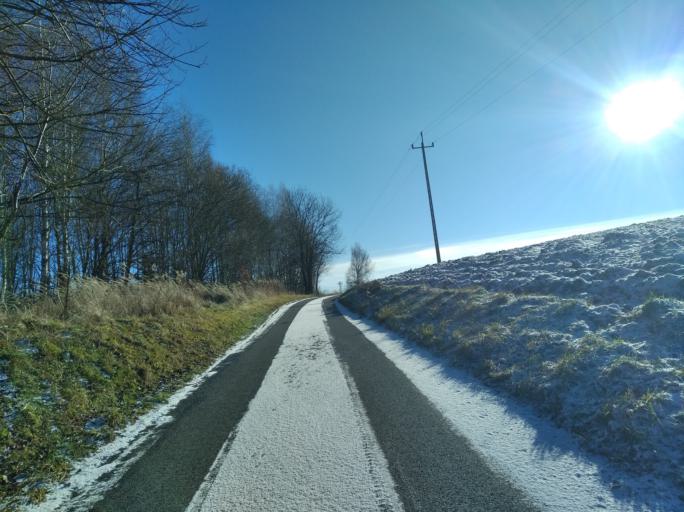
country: PL
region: Subcarpathian Voivodeship
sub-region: Powiat ropczycko-sedziszowski
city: Iwierzyce
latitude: 49.9548
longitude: 21.7589
